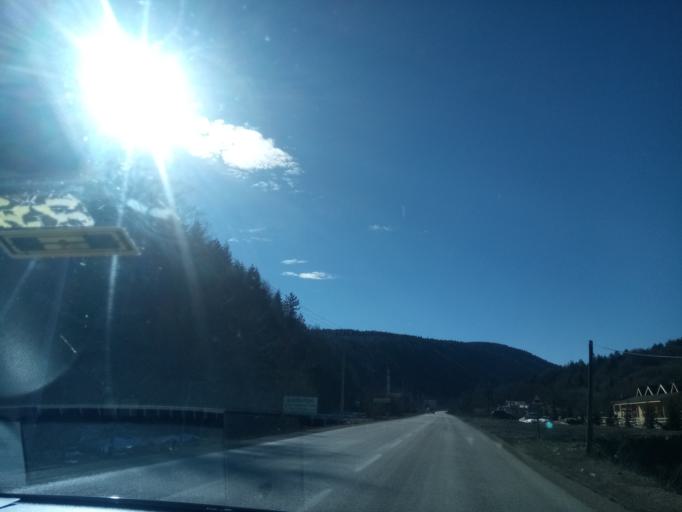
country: TR
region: Duzce
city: Kaynasli
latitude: 40.6655
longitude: 31.4228
